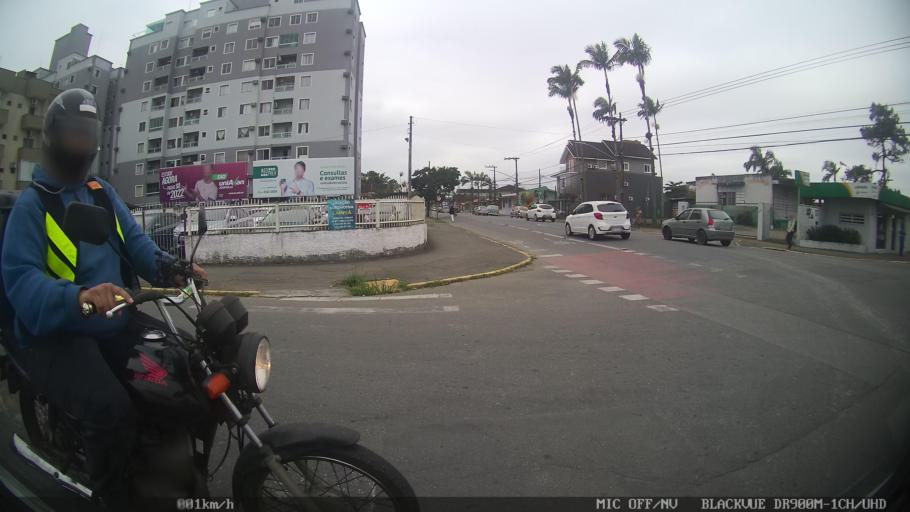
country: BR
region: Santa Catarina
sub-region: Joinville
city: Joinville
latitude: -26.3161
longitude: -48.8393
